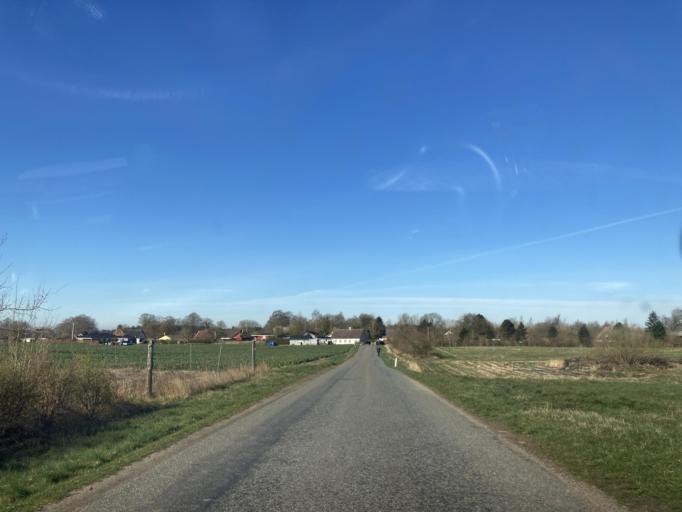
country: DK
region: Zealand
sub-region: Ringsted Kommune
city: Ringsted
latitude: 55.4935
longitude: 11.8258
